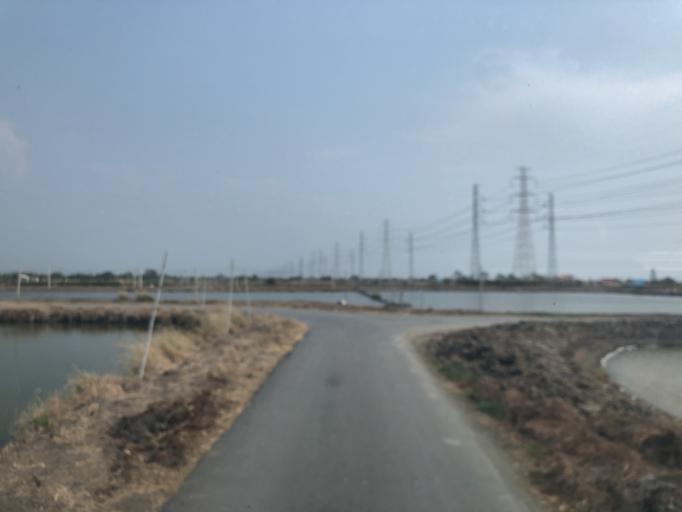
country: TH
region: Samut Prakan
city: Bang Bo
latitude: 13.5437
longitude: 100.8866
